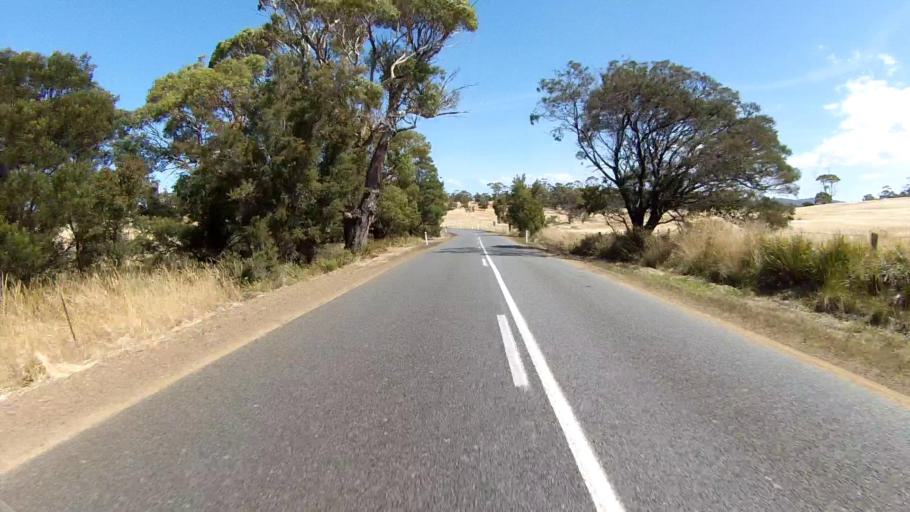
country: AU
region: Tasmania
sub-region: Sorell
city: Sorell
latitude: -42.2799
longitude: 148.0010
